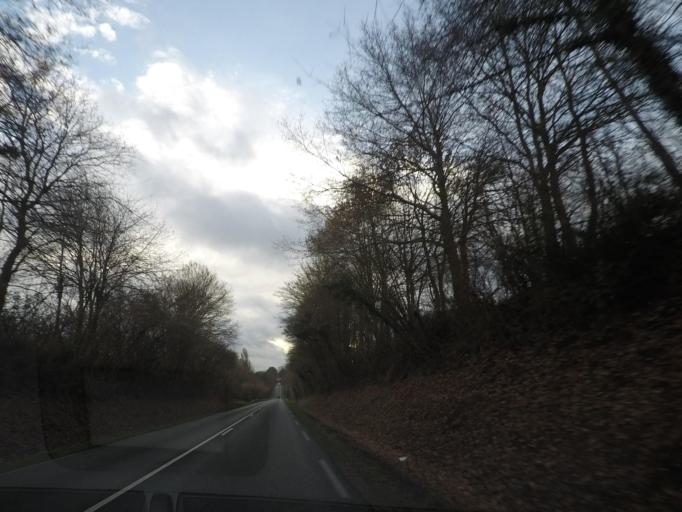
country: FR
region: Pays de la Loire
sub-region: Departement de la Sarthe
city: Cherre
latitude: 48.1362
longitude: 0.6952
